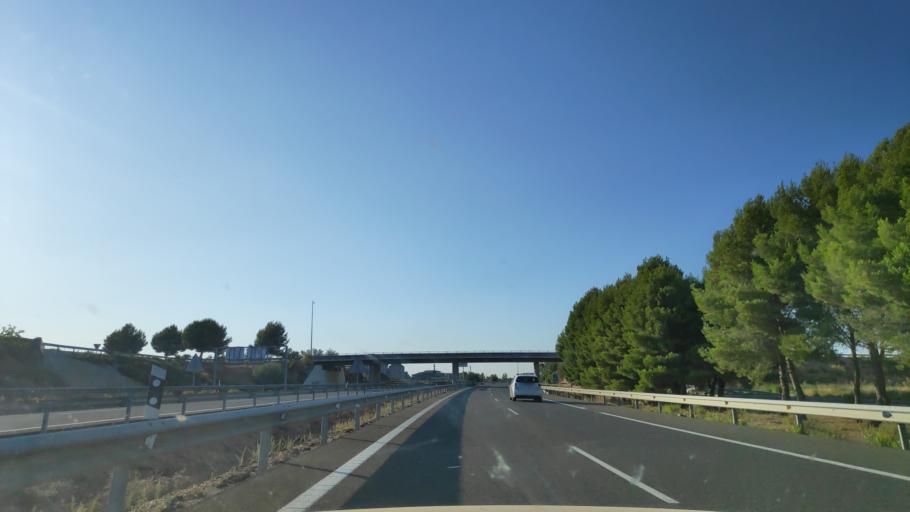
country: ES
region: Castille-La Mancha
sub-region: Provincia de Cuenca
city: Tarancon
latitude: 40.0038
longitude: -3.0264
